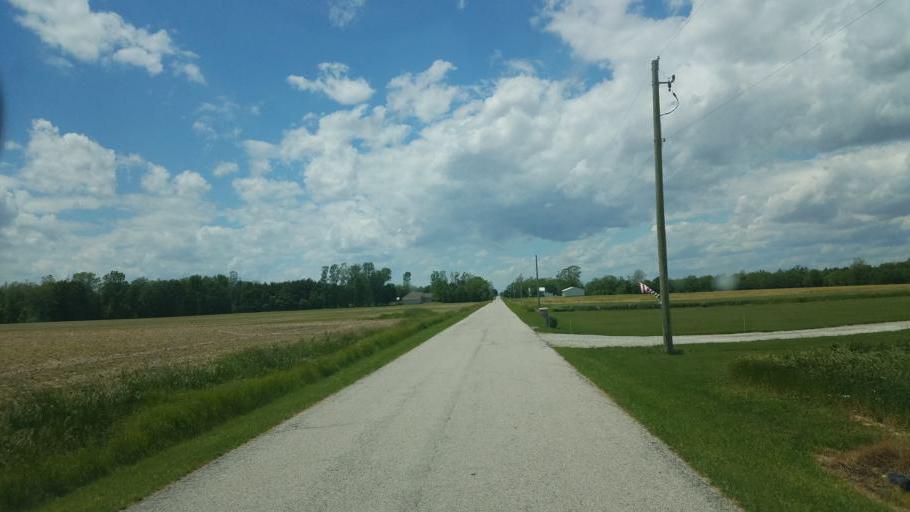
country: US
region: Ohio
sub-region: Huron County
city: Willard
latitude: 41.1428
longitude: -82.7743
